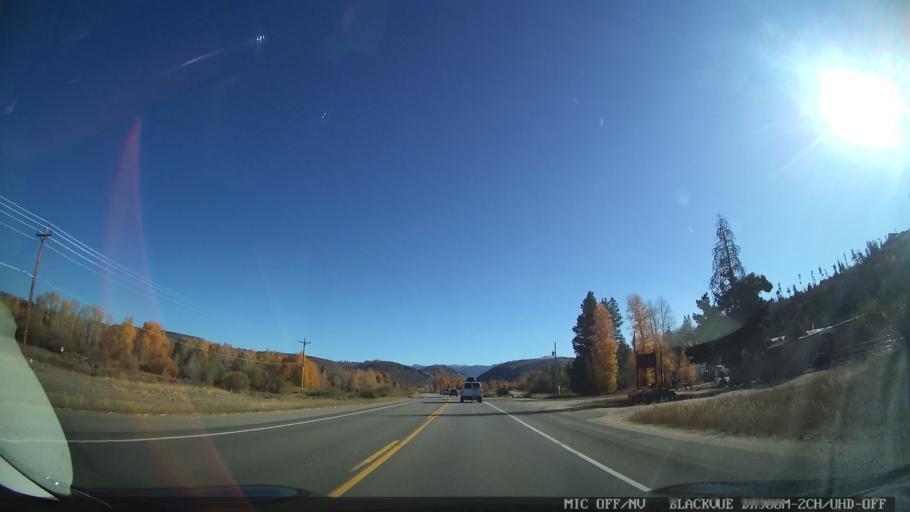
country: US
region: Colorado
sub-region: Grand County
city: Granby
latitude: 40.1160
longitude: -105.9108
